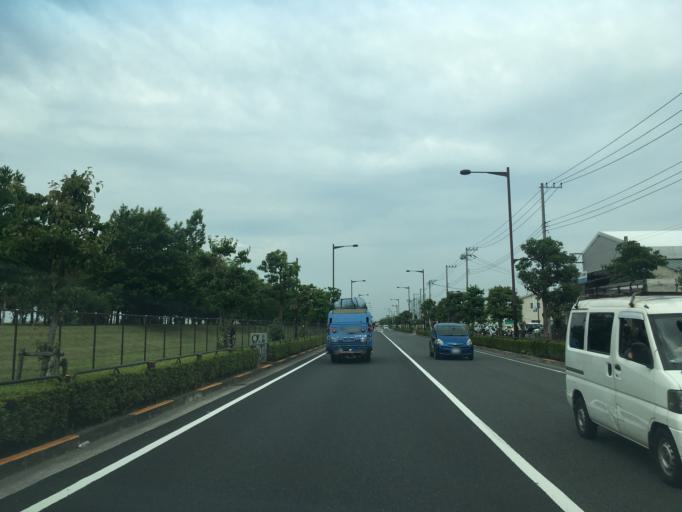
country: JP
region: Tokyo
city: Hino
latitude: 35.7407
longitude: 139.3917
